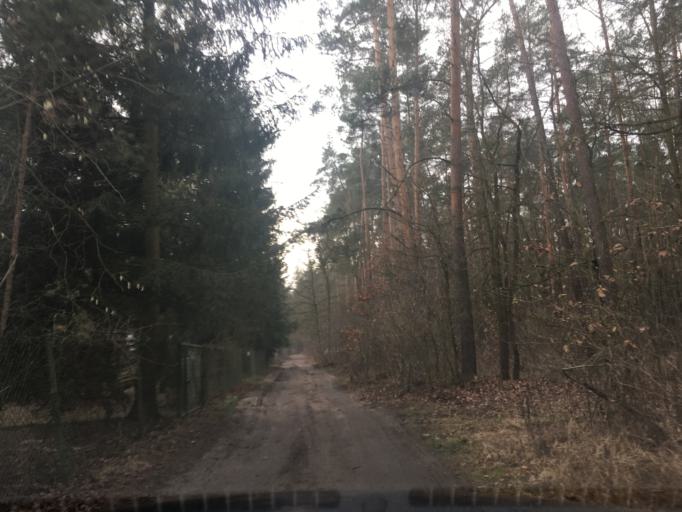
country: PL
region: Masovian Voivodeship
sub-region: Powiat piaseczynski
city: Lesznowola
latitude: 52.0788
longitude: 20.9198
